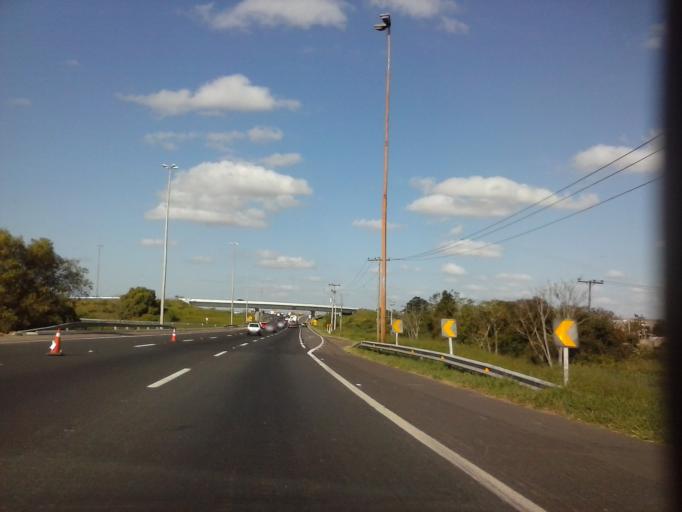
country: BR
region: Rio Grande do Sul
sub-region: Canoas
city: Canoas
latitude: -29.9709
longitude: -51.1842
